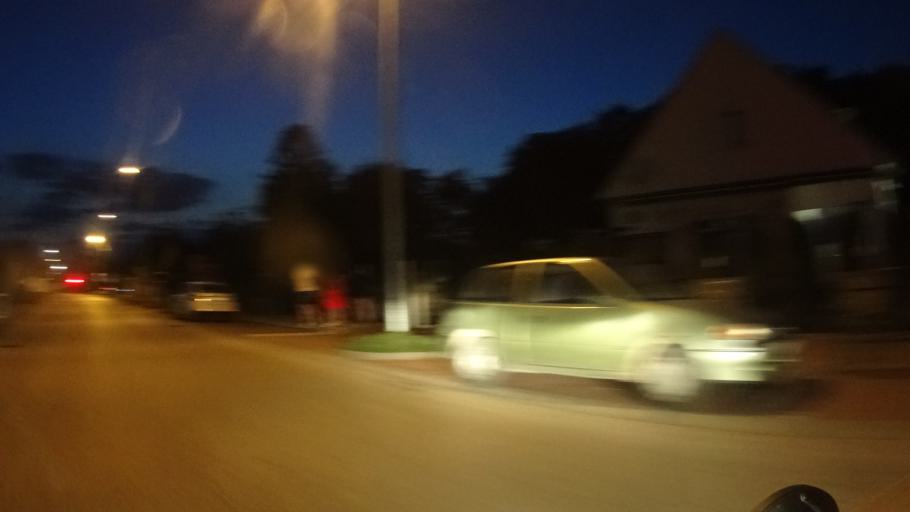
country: HU
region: Somogy
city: Balatonbereny
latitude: 46.7037
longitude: 17.3718
